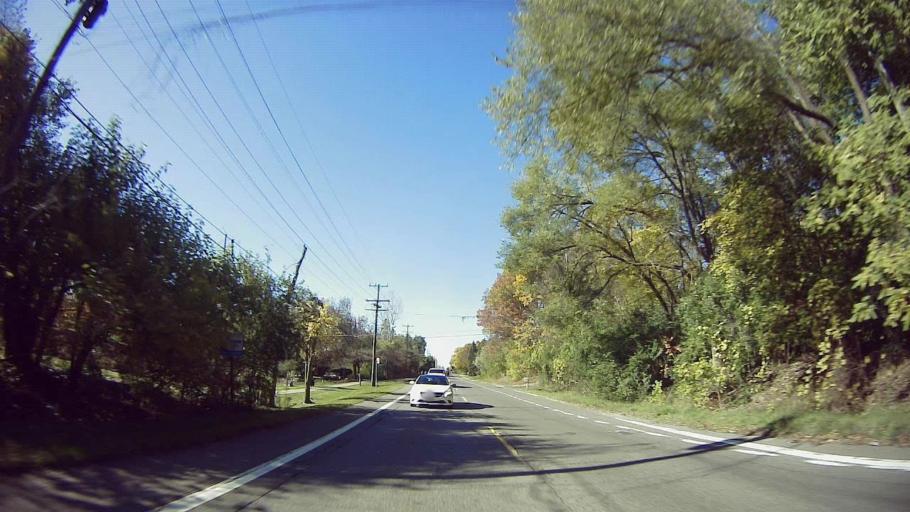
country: US
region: Michigan
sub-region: Oakland County
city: Franklin
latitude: 42.5441
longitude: -83.3153
